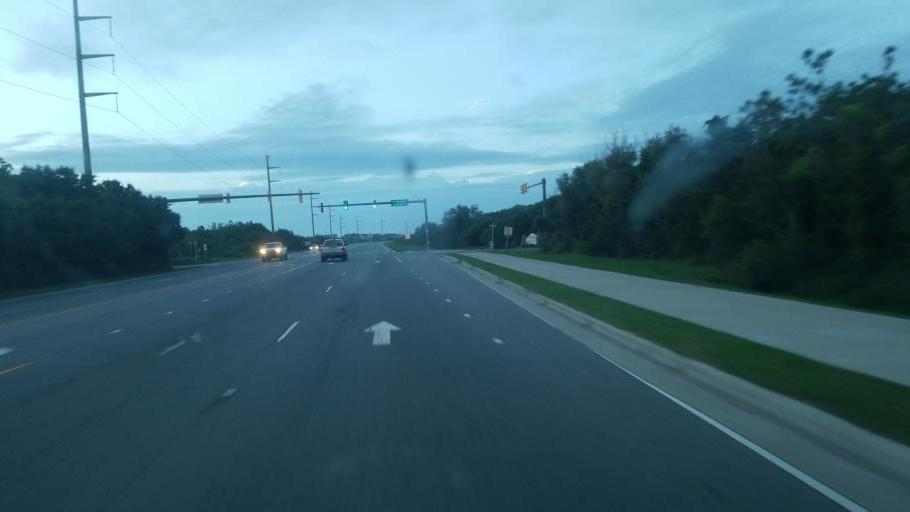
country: US
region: North Carolina
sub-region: Dare County
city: Nags Head
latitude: 35.9676
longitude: -75.6329
